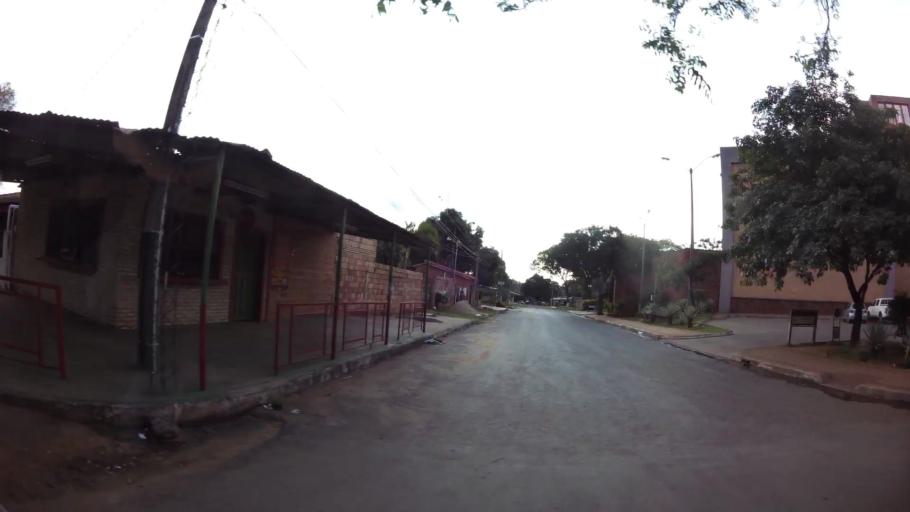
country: PY
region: Central
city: Fernando de la Mora
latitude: -25.3670
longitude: -57.5241
